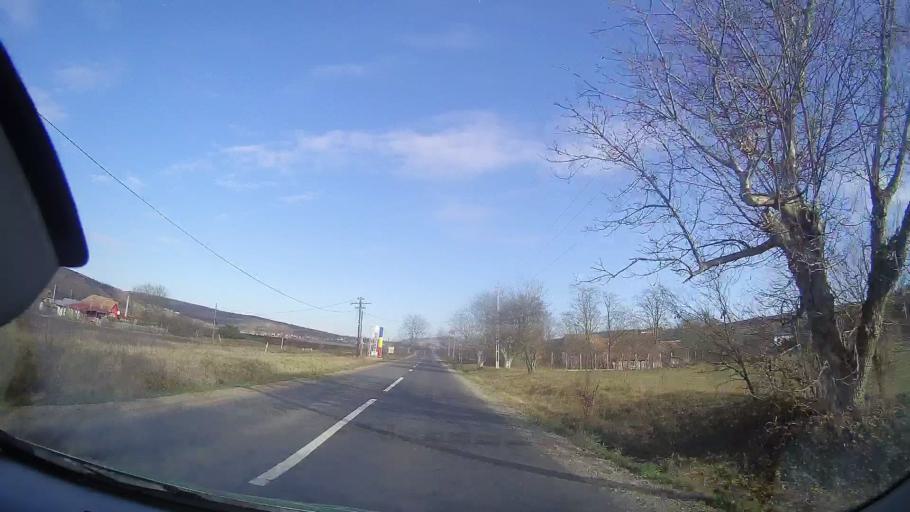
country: RO
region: Mures
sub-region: Comuna Zau De Campie
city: Zau de Campie
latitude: 46.5912
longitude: 24.1059
